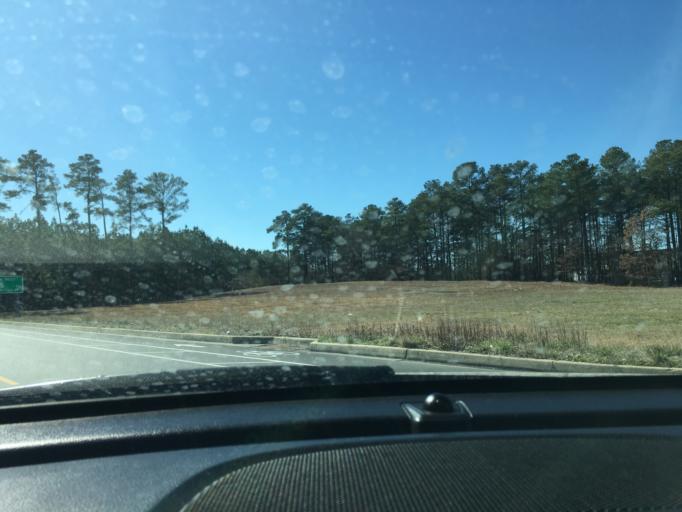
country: US
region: Maryland
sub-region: Wicomico County
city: Salisbury
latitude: 38.4037
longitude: -75.5782
